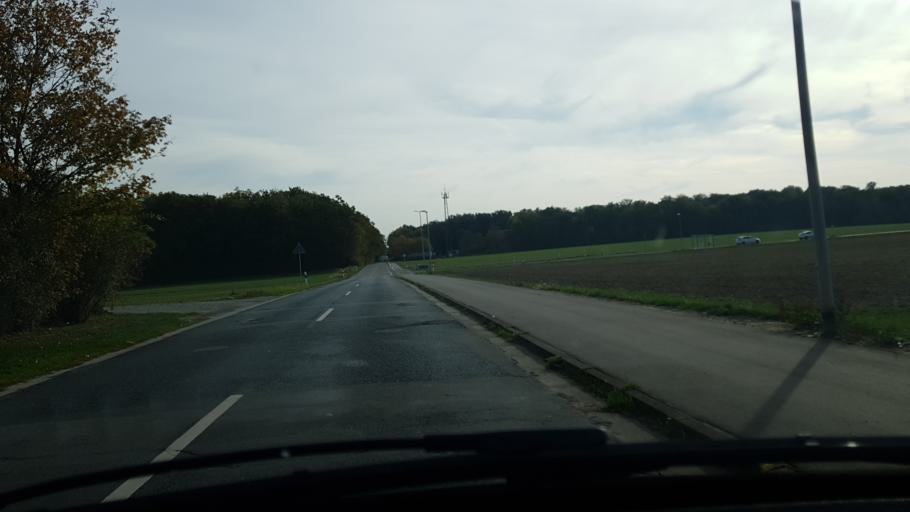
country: DE
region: Lower Saxony
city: Lehre
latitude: 52.3700
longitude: 10.6724
